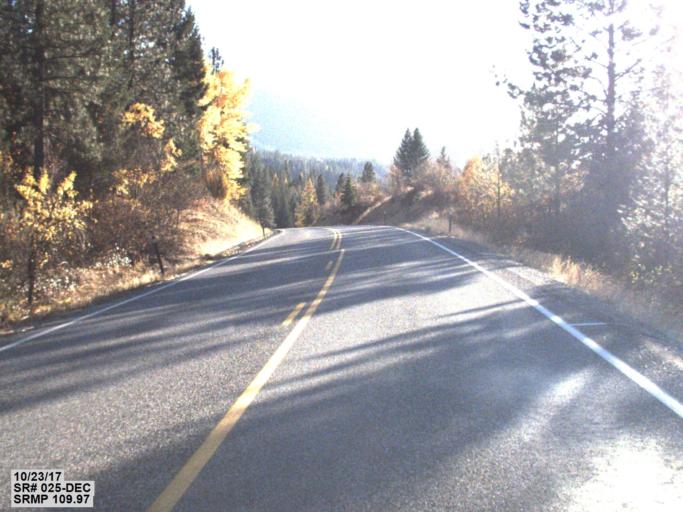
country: CA
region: British Columbia
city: Rossland
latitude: 48.8832
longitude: -117.8325
